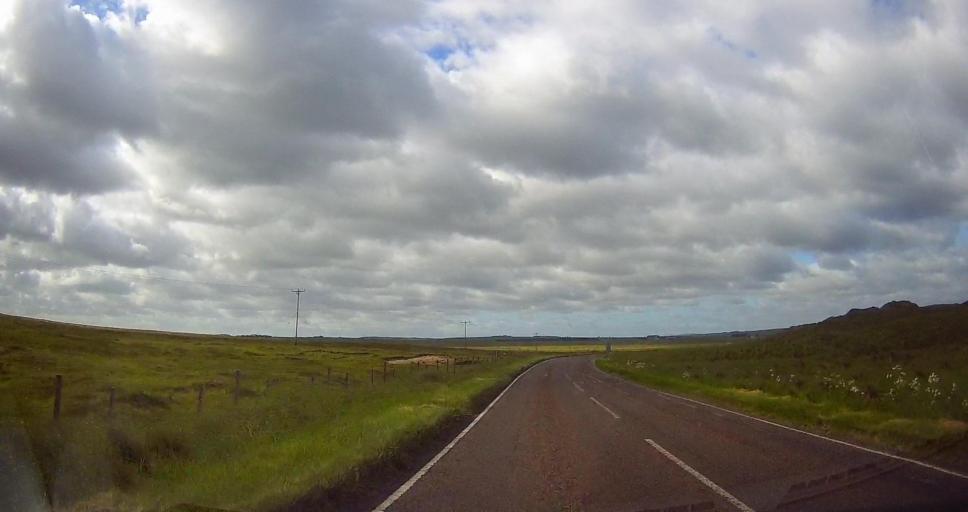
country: GB
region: Scotland
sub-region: Highland
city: Thurso
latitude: 58.6095
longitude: -3.3439
